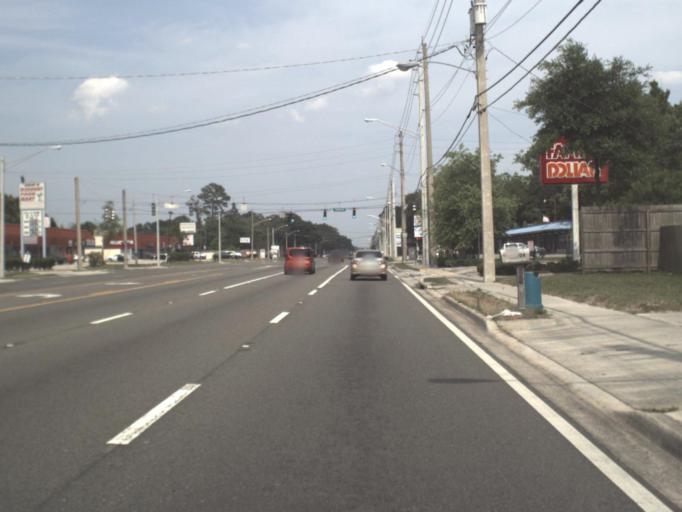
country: US
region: Florida
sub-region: Clay County
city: Bellair-Meadowbrook Terrace
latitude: 30.2472
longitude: -81.7318
